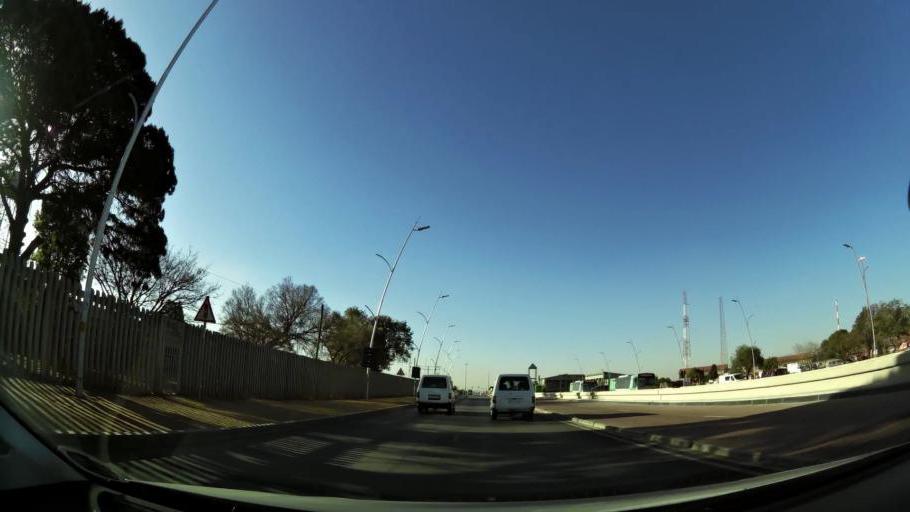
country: ZA
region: Gauteng
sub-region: Ekurhuleni Metropolitan Municipality
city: Tembisa
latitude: -26.0084
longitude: 28.2183
